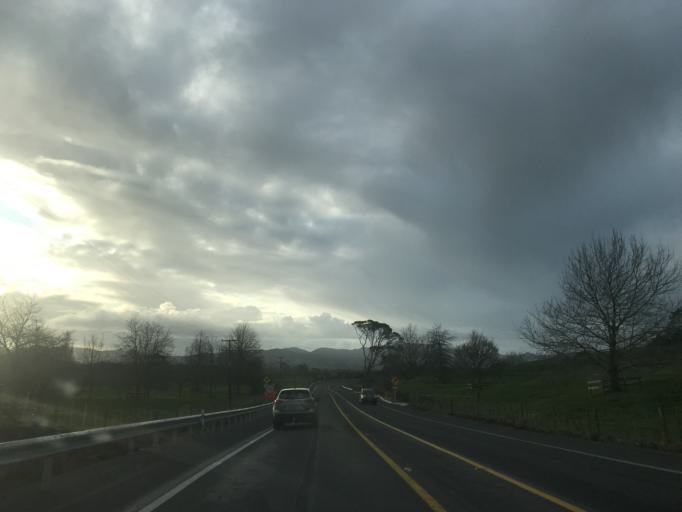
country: NZ
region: Bay of Plenty
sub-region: Western Bay of Plenty District
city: Waihi Beach
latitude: -37.4411
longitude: 175.8751
